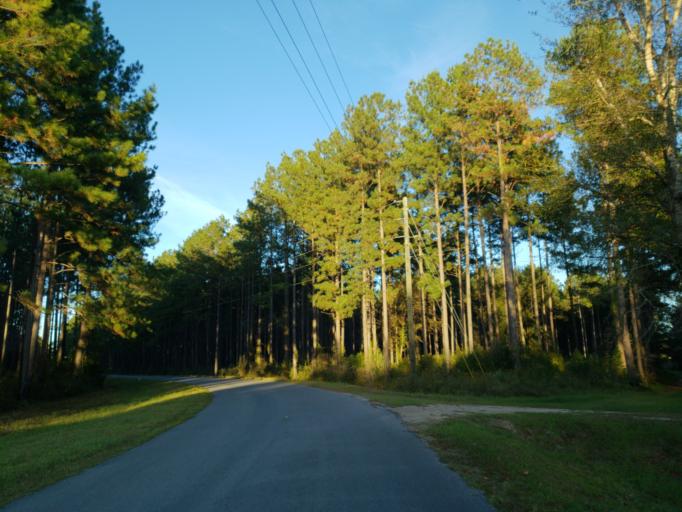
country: US
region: Mississippi
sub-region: Wayne County
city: Belmont
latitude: 31.4541
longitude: -88.5244
